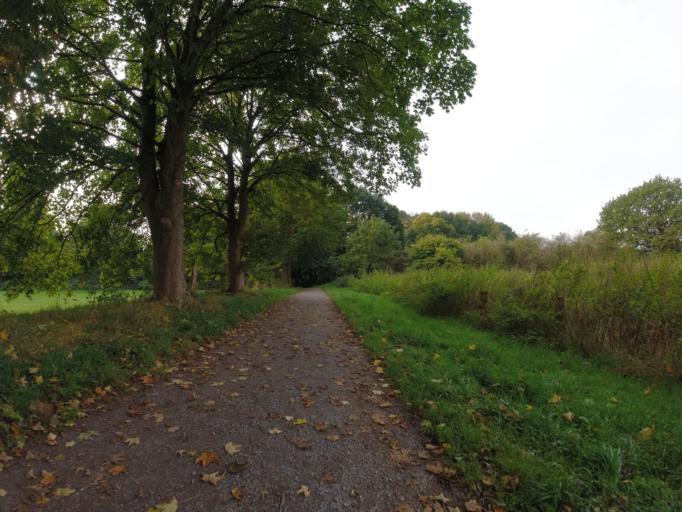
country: DE
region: North Rhine-Westphalia
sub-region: Regierungsbezirk Dusseldorf
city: Hochfeld
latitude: 51.3758
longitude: 6.6902
